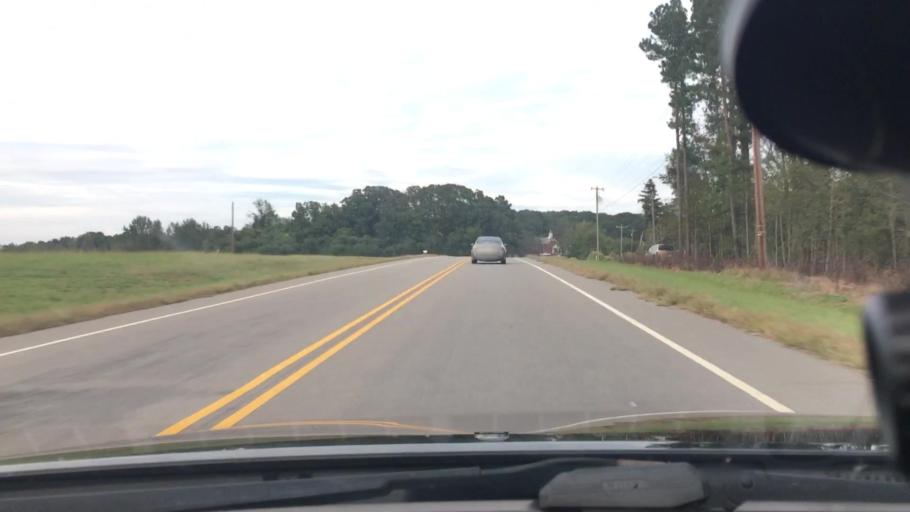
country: US
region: North Carolina
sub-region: Lee County
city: Sanford
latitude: 35.3853
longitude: -79.2743
